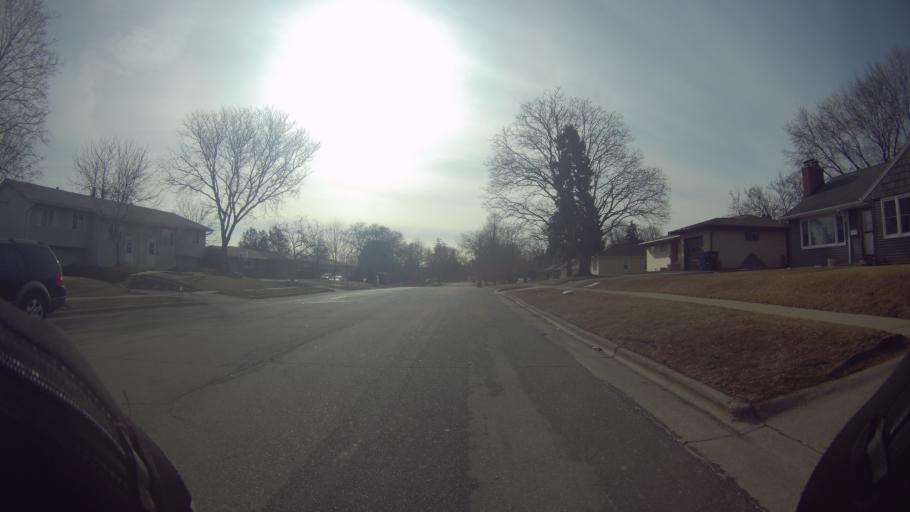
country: US
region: Wisconsin
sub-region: Dane County
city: Middleton
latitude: 43.0953
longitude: -89.4964
